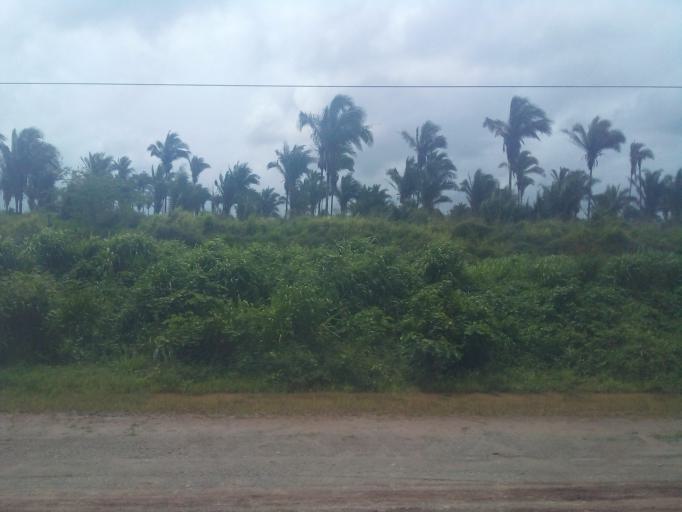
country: BR
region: Maranhao
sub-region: Arari
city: Arari
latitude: -3.5537
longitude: -44.6653
